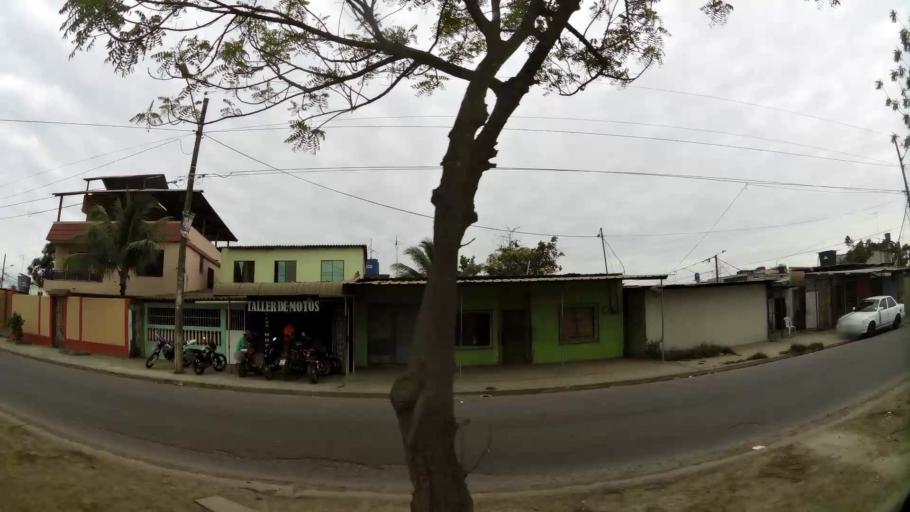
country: EC
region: El Oro
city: Machala
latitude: -3.2454
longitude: -79.9528
